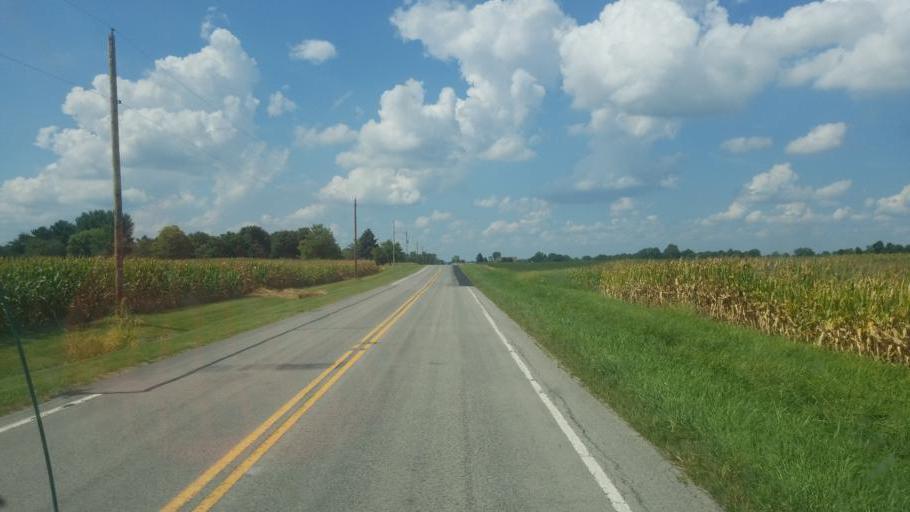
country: US
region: Ohio
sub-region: Hardin County
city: Ada
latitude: 40.7325
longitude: -83.7041
